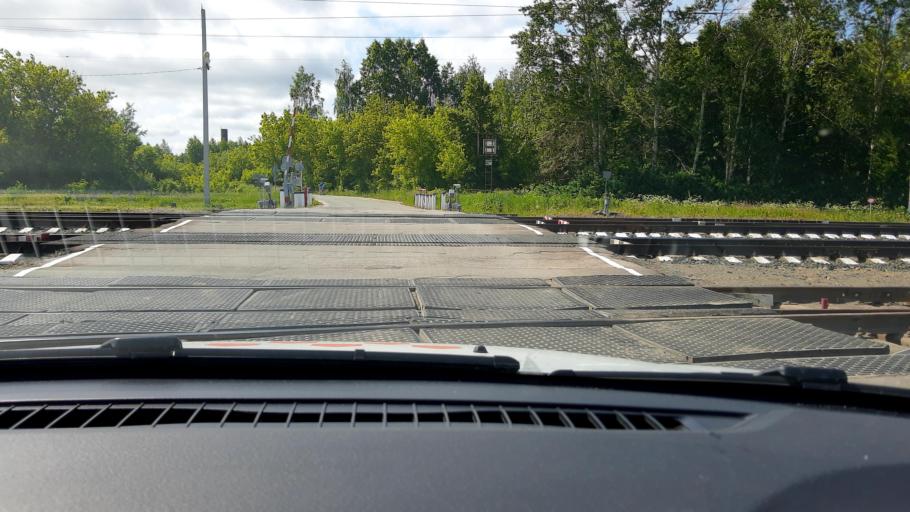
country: RU
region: Nizjnij Novgorod
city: Linda
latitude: 56.5507
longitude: 44.0632
